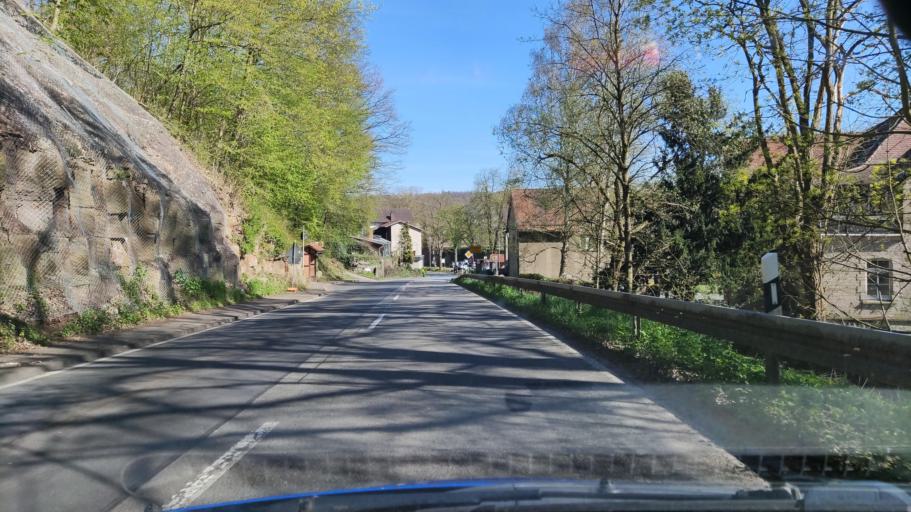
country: DE
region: Lower Saxony
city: Bad Karlshafen
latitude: 51.6313
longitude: 9.4512
